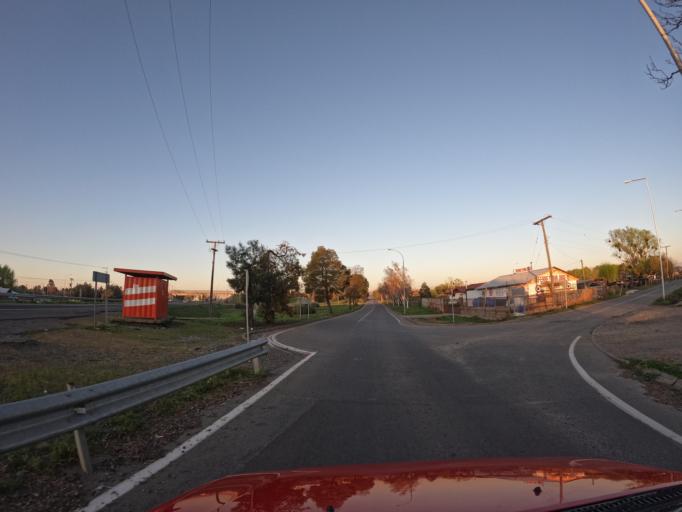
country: CL
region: Biobio
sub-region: Provincia de Nuble
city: San Carlos
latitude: -36.3636
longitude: -71.8808
